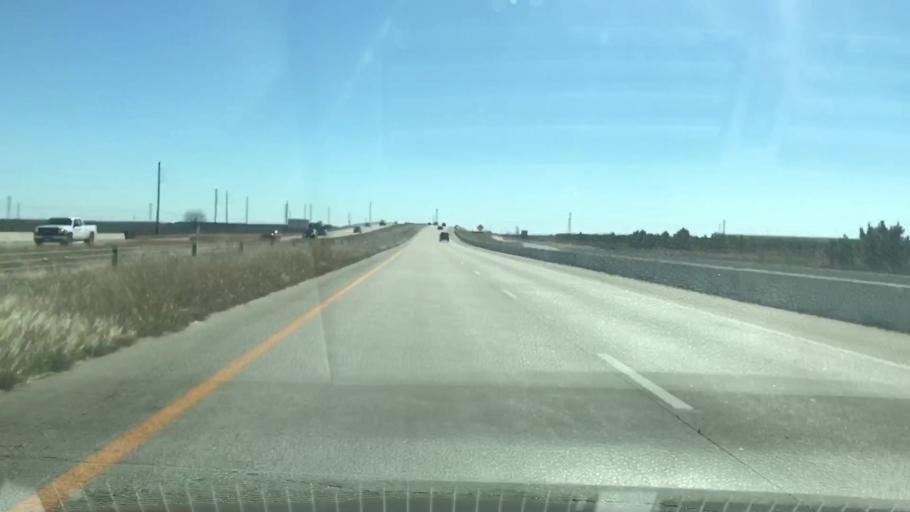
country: US
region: Texas
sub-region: Harris County
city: Cypress
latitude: 29.9266
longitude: -95.7627
